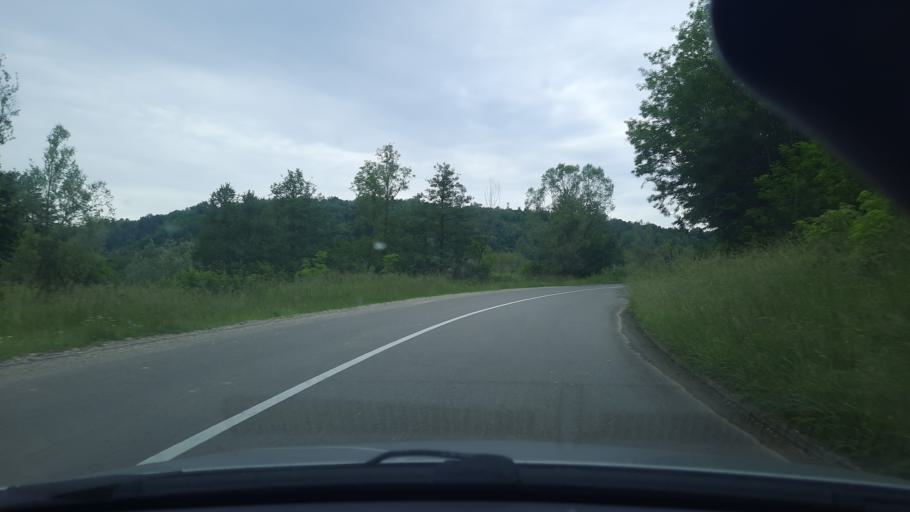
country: RS
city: Bukor
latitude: 44.5050
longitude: 19.4979
